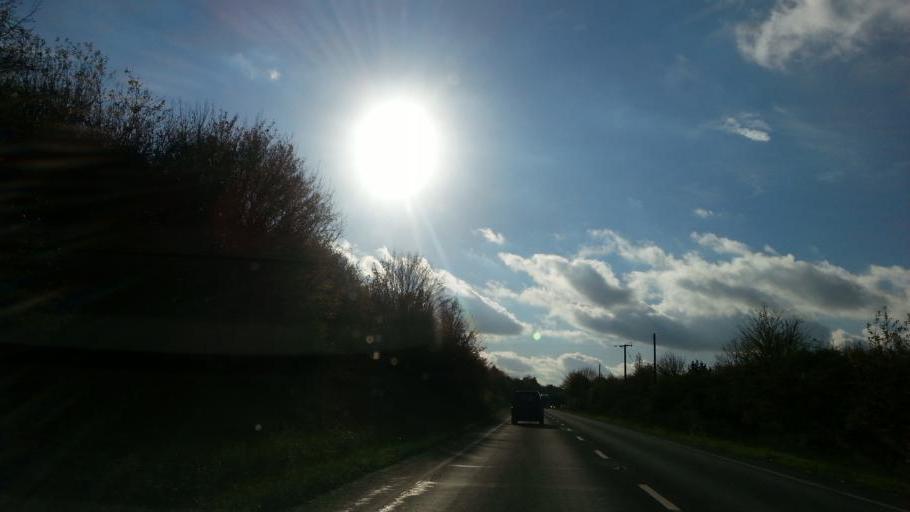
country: GB
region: England
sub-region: Norfolk
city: Harleston
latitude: 52.3790
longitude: 1.2548
